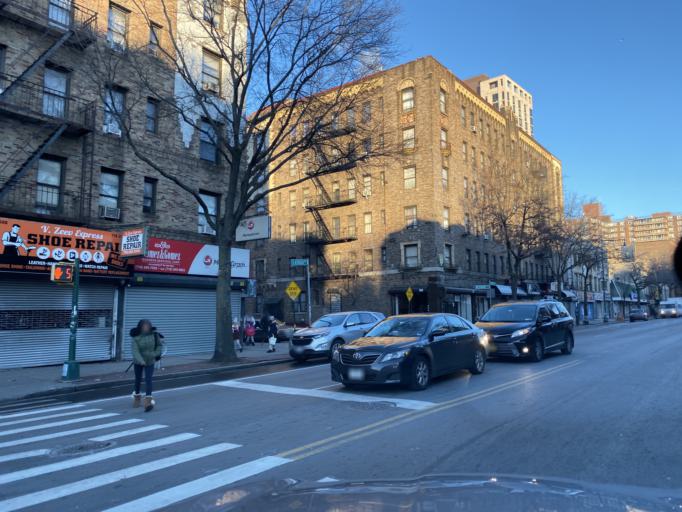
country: US
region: New York
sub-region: Kings County
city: Brooklyn
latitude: 40.6566
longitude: -73.9600
